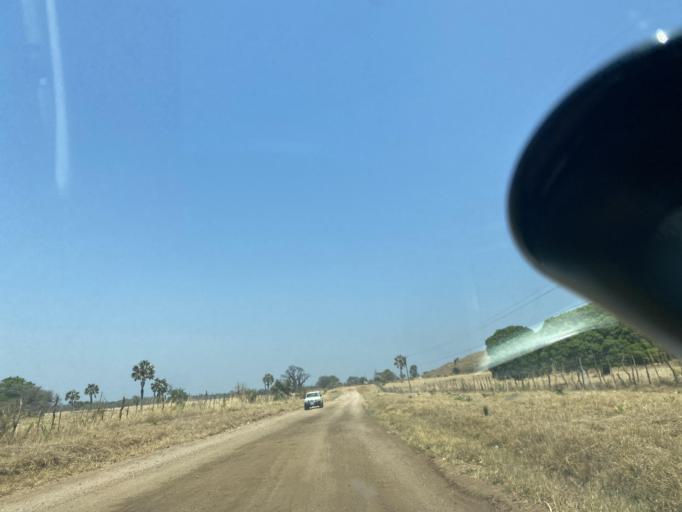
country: ZM
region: Lusaka
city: Lusaka
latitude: -15.5355
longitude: 28.0886
